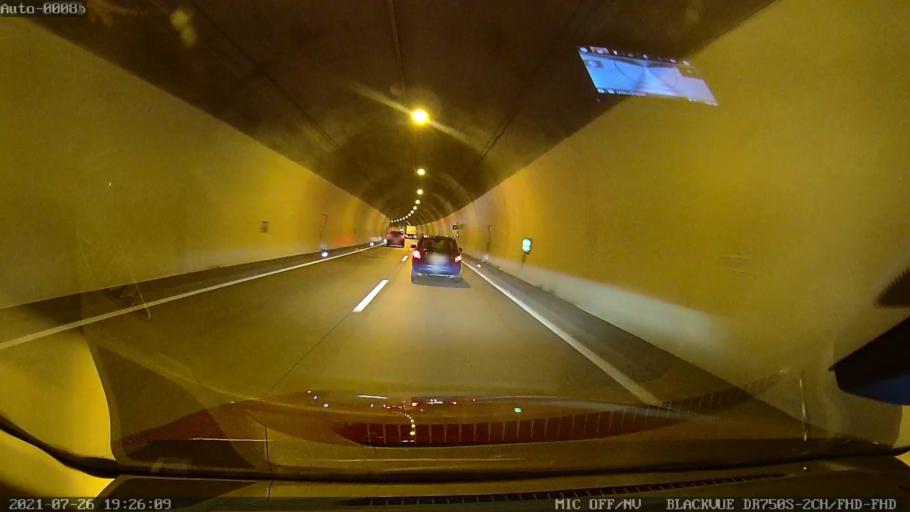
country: AT
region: Upper Austria
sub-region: Politischer Bezirk Kirchdorf an der Krems
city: Micheldorf in Oberoesterreich
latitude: 47.8561
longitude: 14.1572
